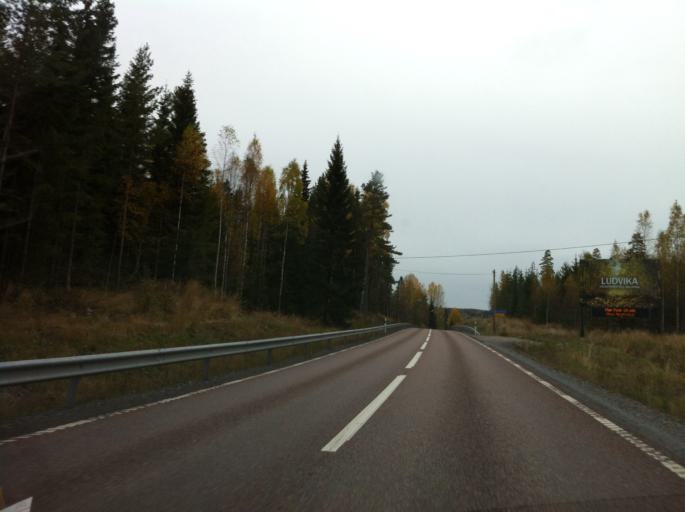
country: SE
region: Dalarna
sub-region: Ludvika Kommun
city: Grangesberg
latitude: 60.0514
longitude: 14.9841
